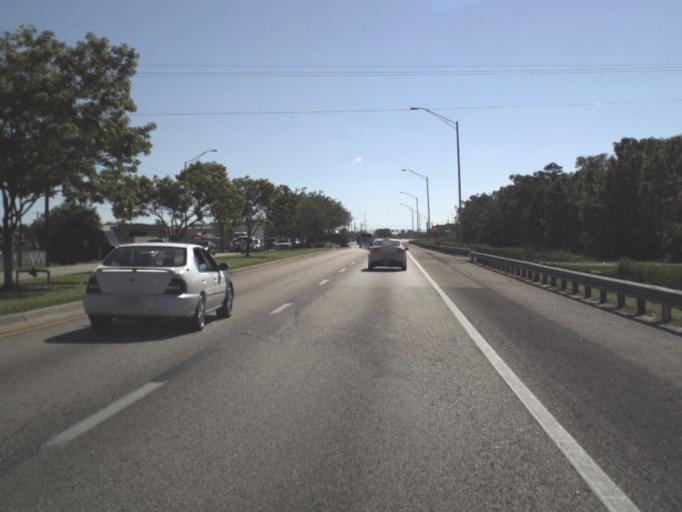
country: US
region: Florida
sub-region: Lee County
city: Fort Myers
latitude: 26.6399
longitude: -81.8183
